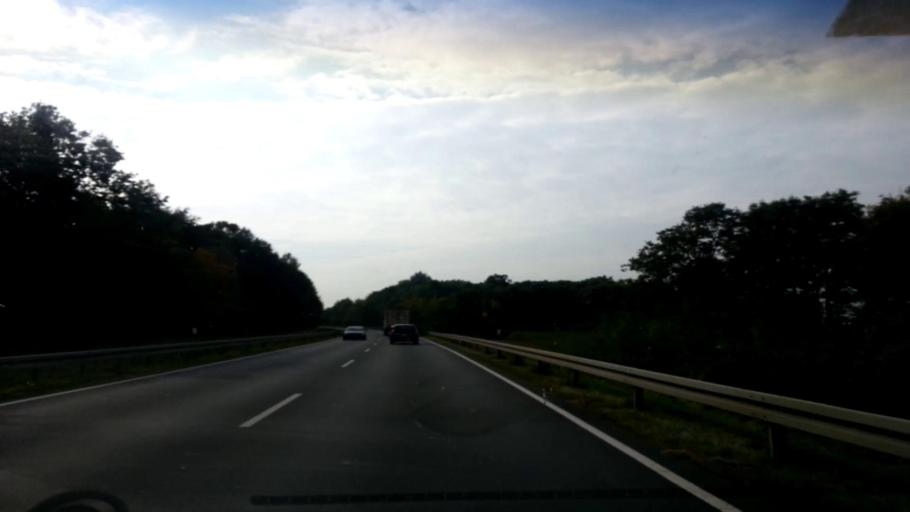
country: DE
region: Bavaria
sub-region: Regierungsbezirk Unterfranken
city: Prichsenstadt
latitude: 49.8335
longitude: 10.3536
